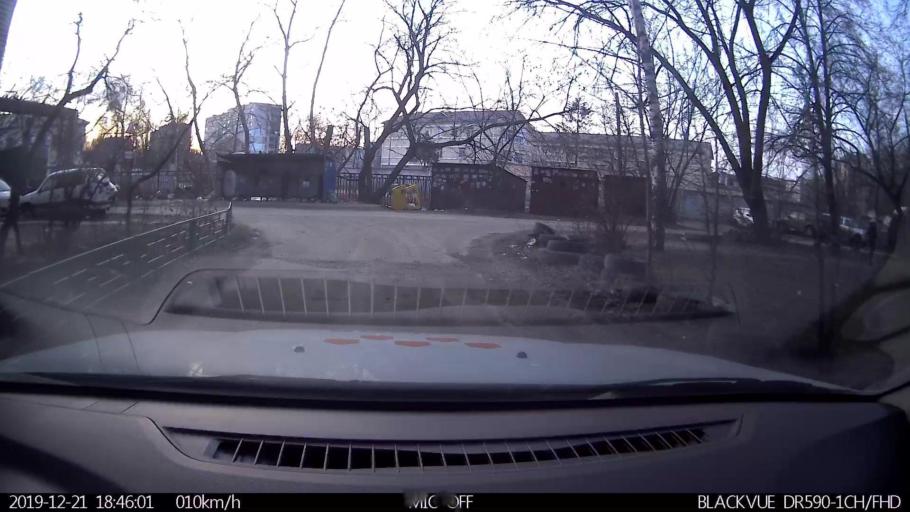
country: RU
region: Nizjnij Novgorod
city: Nizhniy Novgorod
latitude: 56.3289
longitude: 43.9202
